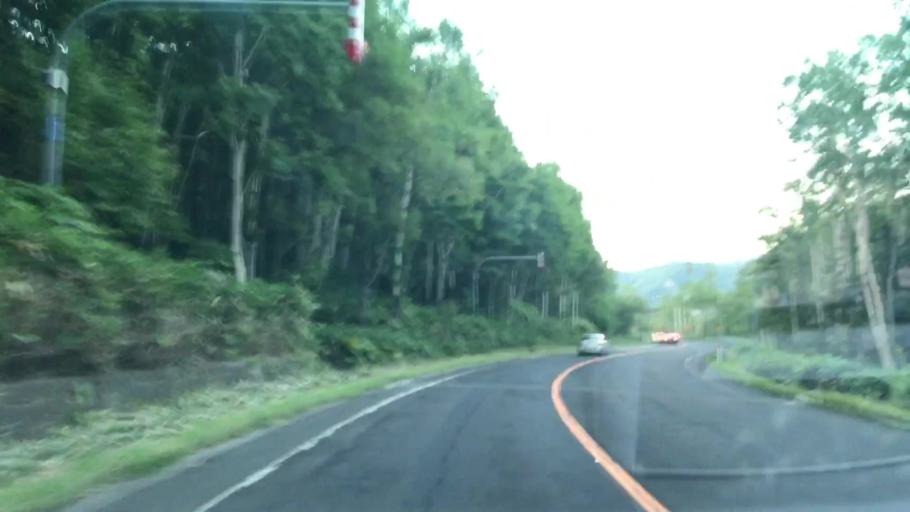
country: JP
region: Hokkaido
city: Sapporo
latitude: 42.8841
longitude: 141.1402
